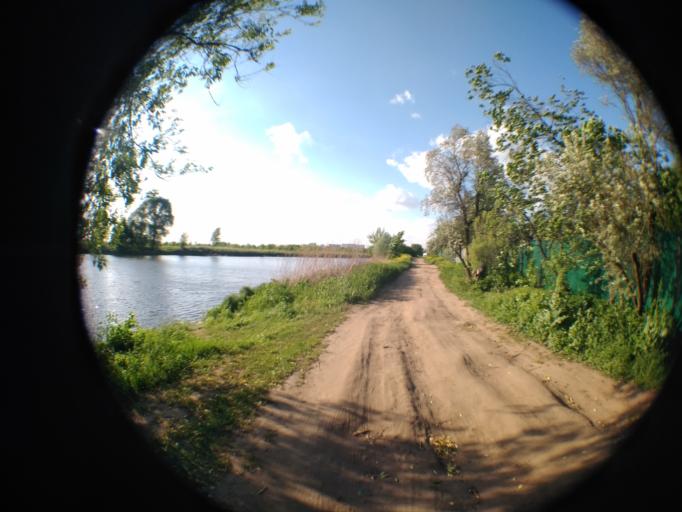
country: RU
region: Moskovskaya
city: Zhukovskiy
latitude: 55.5781
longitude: 38.1026
